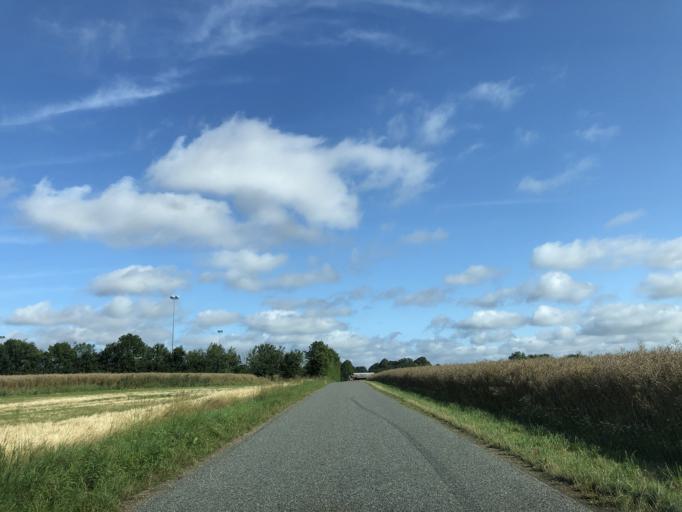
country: DK
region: Central Jutland
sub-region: Silkeborg Kommune
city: Svejbaek
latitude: 56.2216
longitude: 9.6357
